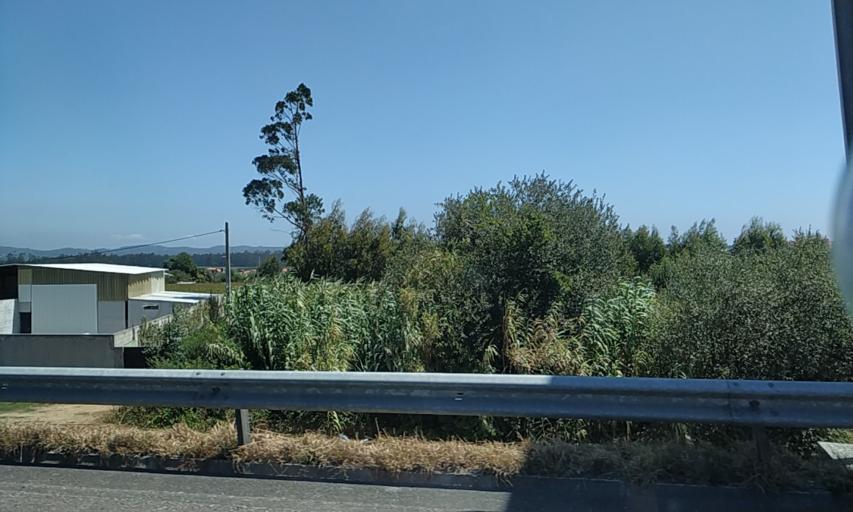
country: PT
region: Porto
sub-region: Matosinhos
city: Lavra
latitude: 41.2650
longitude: -8.7015
